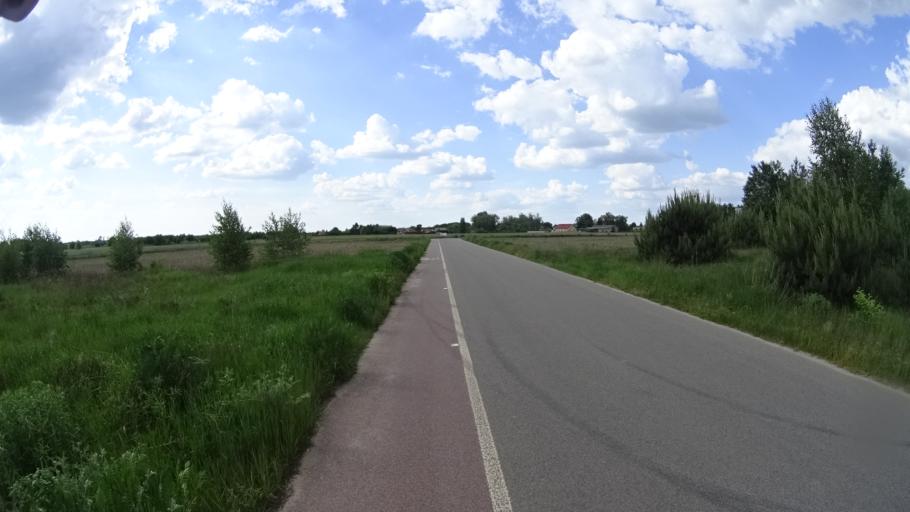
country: PL
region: Masovian Voivodeship
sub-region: Powiat piaseczynski
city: Tarczyn
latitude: 52.0041
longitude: 20.8308
